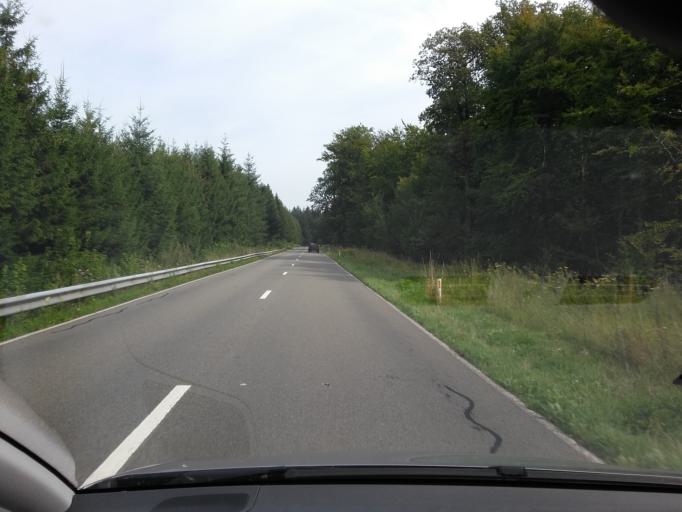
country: BE
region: Wallonia
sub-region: Province du Luxembourg
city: Chiny
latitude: 49.7702
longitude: 5.3240
